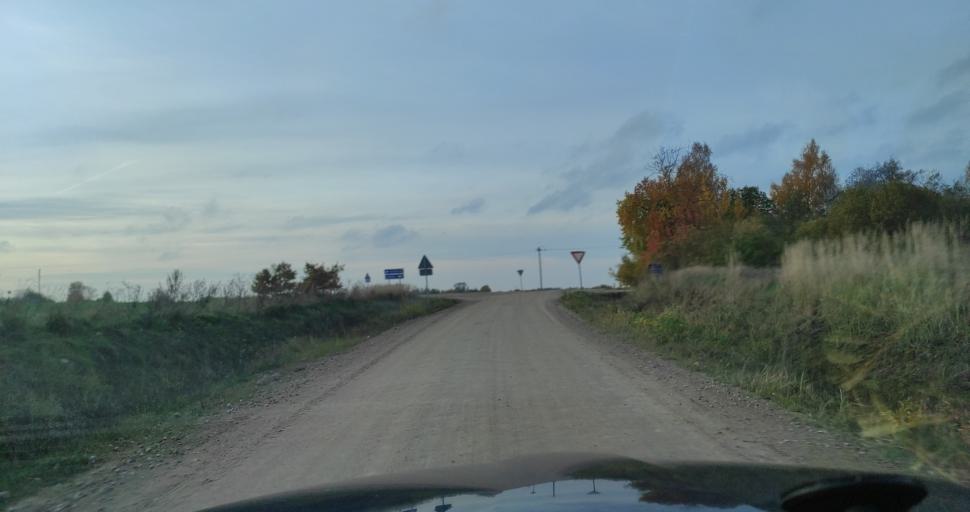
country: LV
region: Skrunda
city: Skrunda
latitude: 56.6393
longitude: 21.8095
